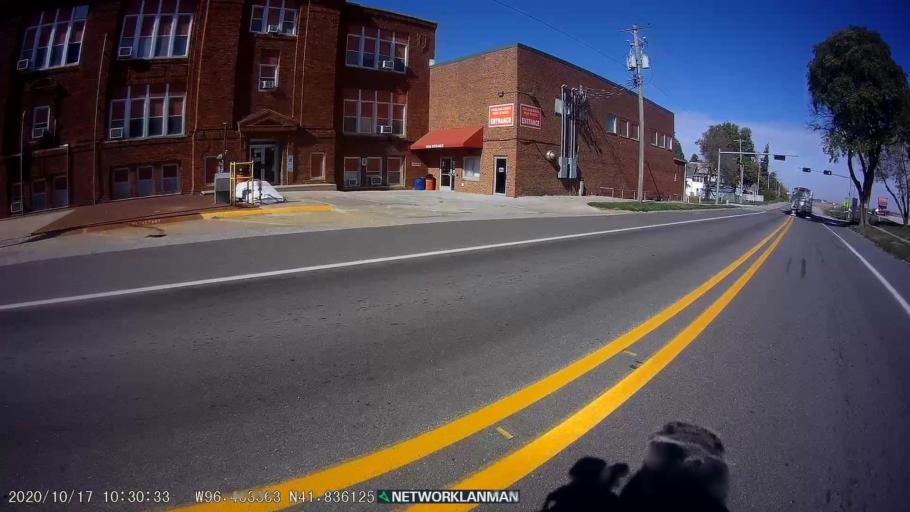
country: US
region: Nebraska
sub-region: Burt County
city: Oakland
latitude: 41.8363
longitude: -96.4635
